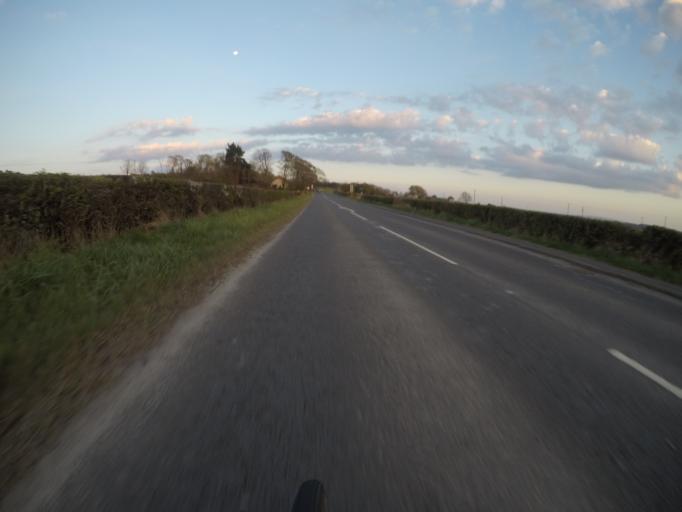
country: GB
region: Scotland
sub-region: South Ayrshire
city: Troon
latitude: 55.5571
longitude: -4.6273
